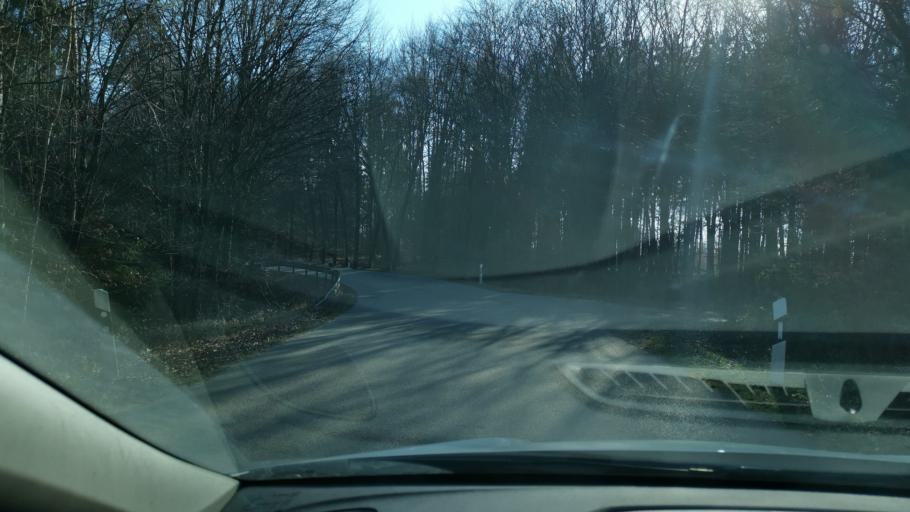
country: DE
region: Bavaria
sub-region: Swabia
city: Aindling
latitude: 48.5432
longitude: 10.9651
